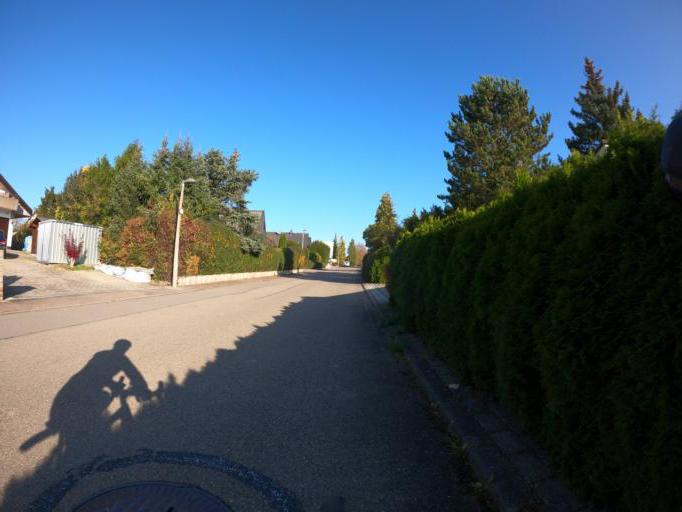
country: DE
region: Baden-Wuerttemberg
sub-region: Regierungsbezirk Stuttgart
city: Aidlingen
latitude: 48.7189
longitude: 8.9095
